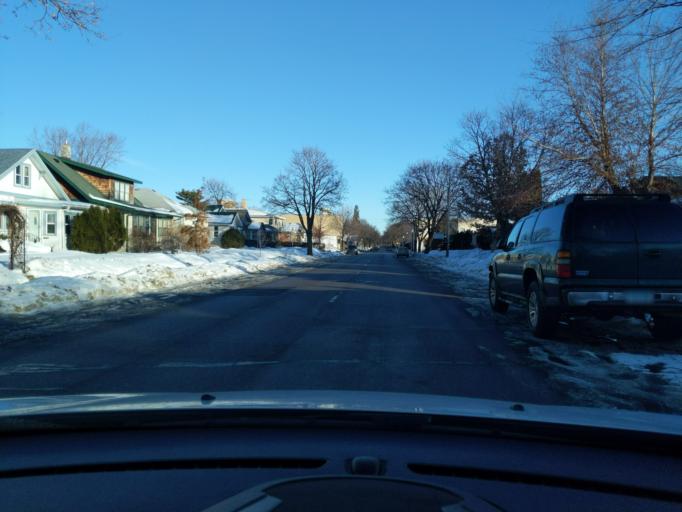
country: US
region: Minnesota
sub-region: Ramsey County
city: Lauderdale
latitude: 44.9327
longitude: -93.2128
